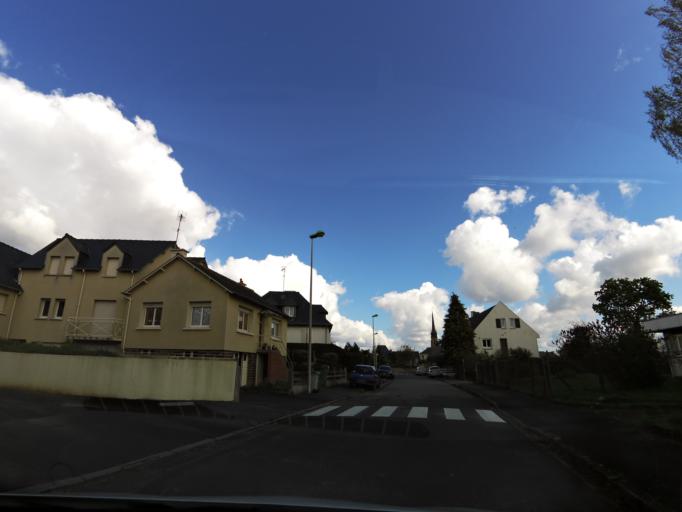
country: FR
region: Brittany
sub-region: Departement d'Ille-et-Vilaine
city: Saint-Erblon
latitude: 48.0176
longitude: -1.6521
